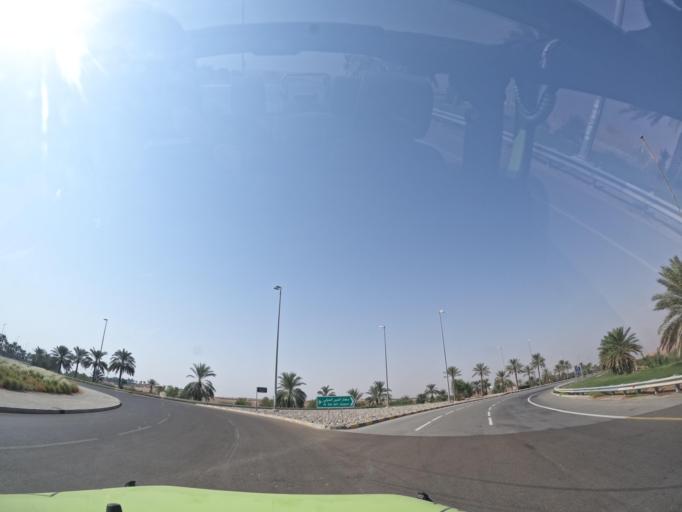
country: AE
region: Abu Dhabi
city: Al Ain
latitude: 24.2631
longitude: 55.6688
